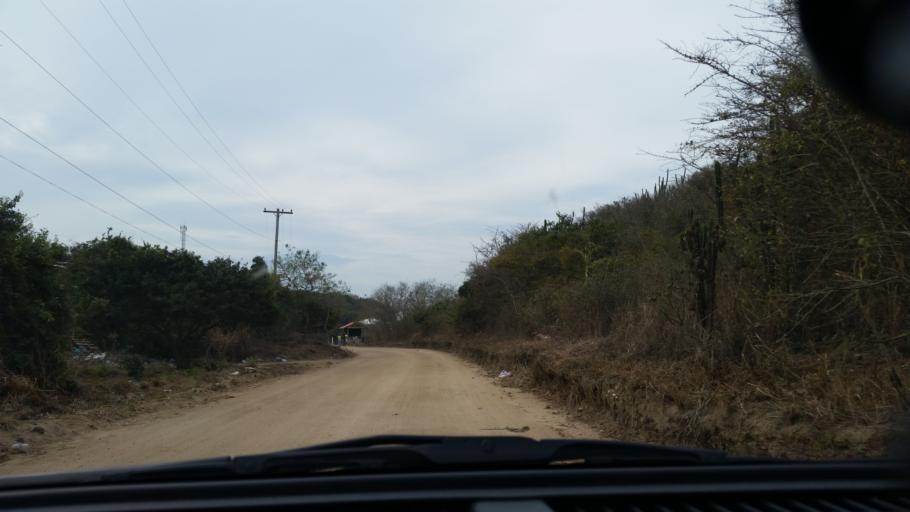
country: BR
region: Rio de Janeiro
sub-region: Cabo Frio
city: Cabo Frio
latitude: -22.8690
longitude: -41.9949
